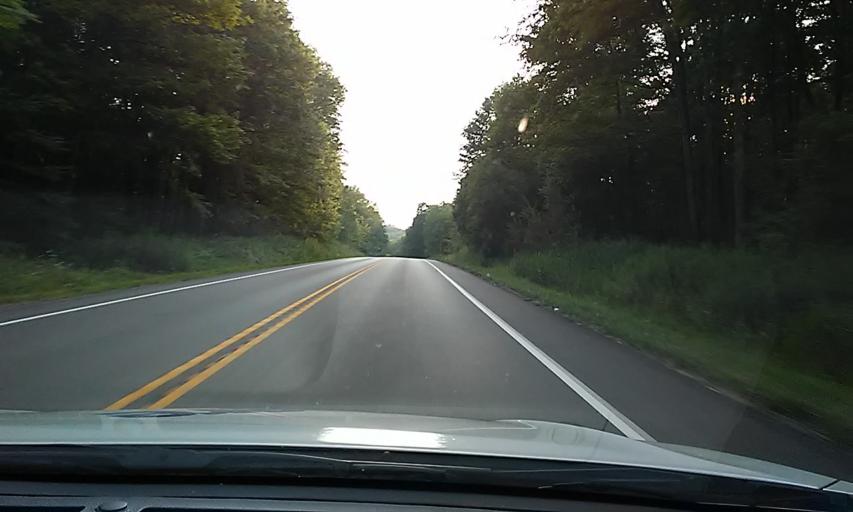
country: US
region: Pennsylvania
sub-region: Forest County
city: Marienville
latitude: 41.5456
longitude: -79.0291
